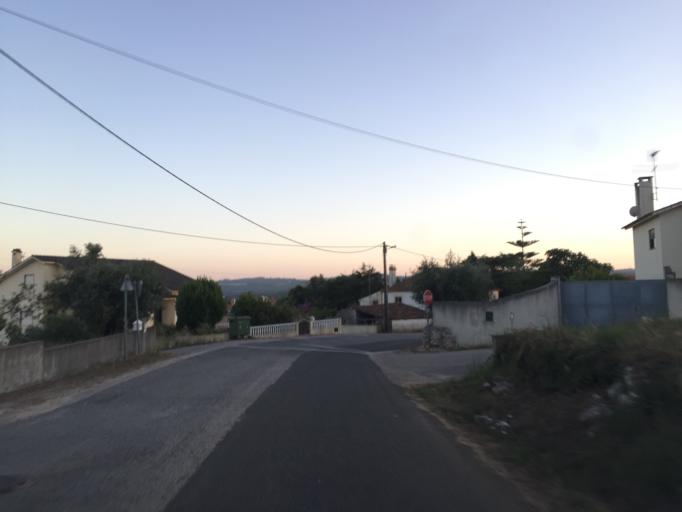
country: PT
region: Santarem
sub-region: Ourem
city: Fatima
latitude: 39.6194
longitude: -8.6499
